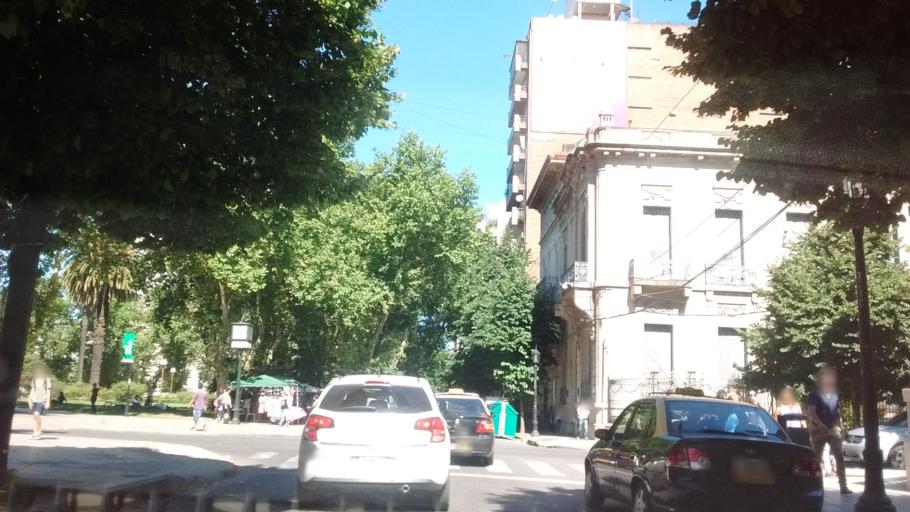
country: AR
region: Santa Fe
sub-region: Departamento de Rosario
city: Rosario
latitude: -32.9441
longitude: -60.6508
